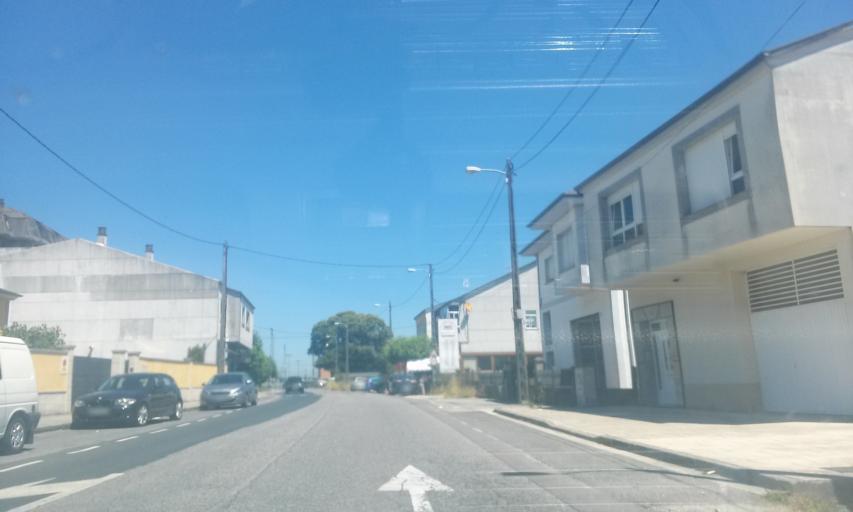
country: ES
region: Galicia
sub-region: Provincia de Lugo
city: Lugo
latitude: 43.0297
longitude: -7.5496
